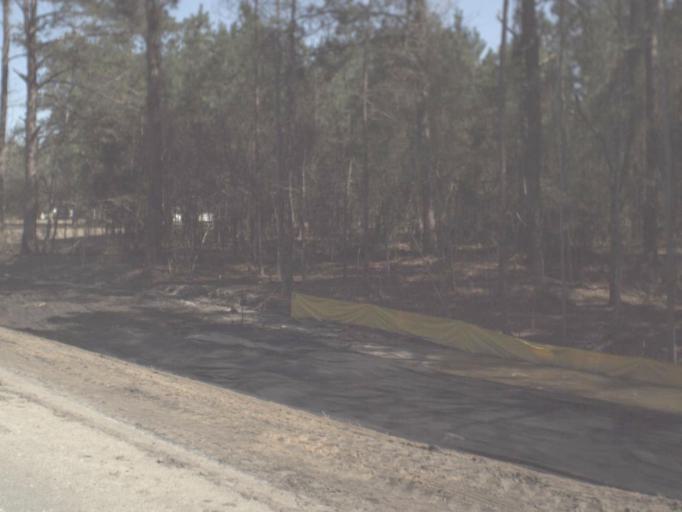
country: US
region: Florida
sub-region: Calhoun County
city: Blountstown
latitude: 30.5297
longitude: -85.0297
